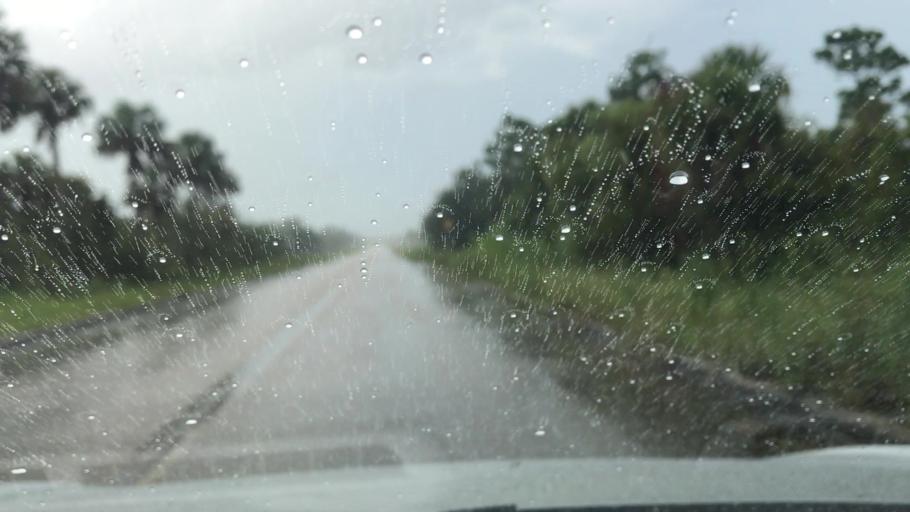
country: US
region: Florida
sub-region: Indian River County
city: Roseland
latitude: 27.8105
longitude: -80.5019
